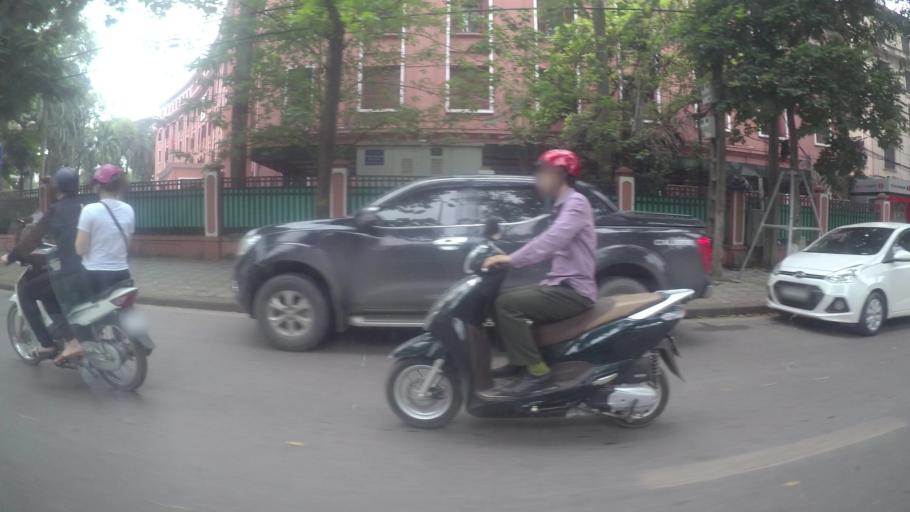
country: VN
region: Ha Noi
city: Hanoi
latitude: 21.0391
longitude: 105.8396
